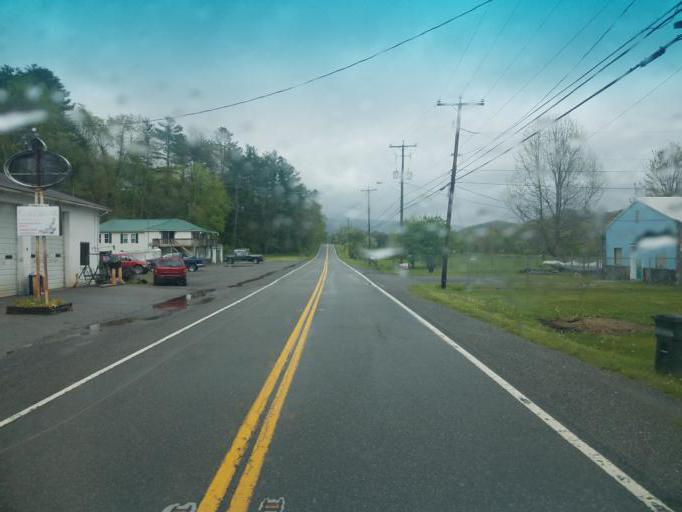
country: US
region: Virginia
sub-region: Bland County
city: Bland
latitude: 37.1630
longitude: -81.1476
